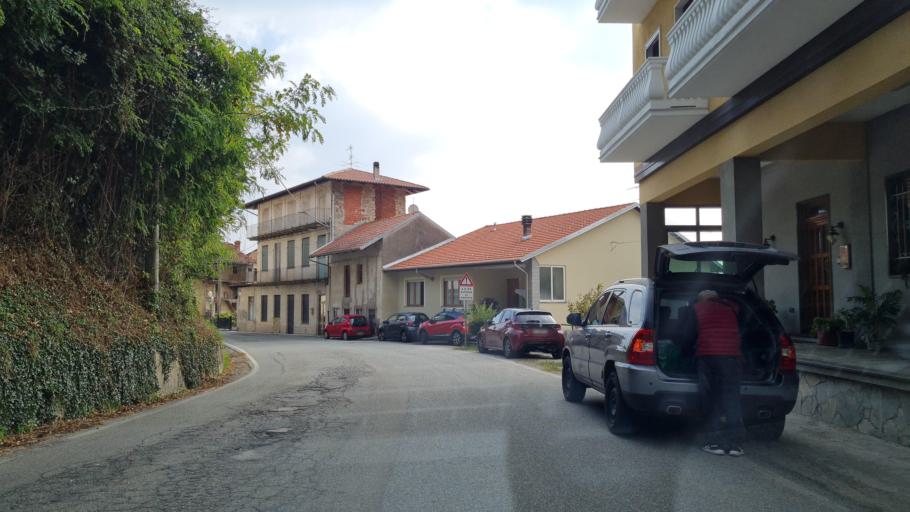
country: IT
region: Piedmont
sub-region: Provincia di Biella
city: Mezzana Mortigliengo
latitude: 45.6267
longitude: 8.1889
